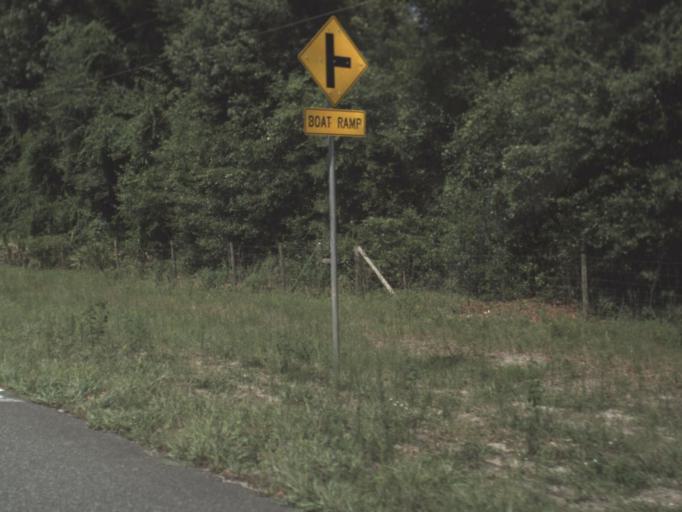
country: US
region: Florida
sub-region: Alachua County
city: High Springs
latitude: 29.8614
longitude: -82.7416
